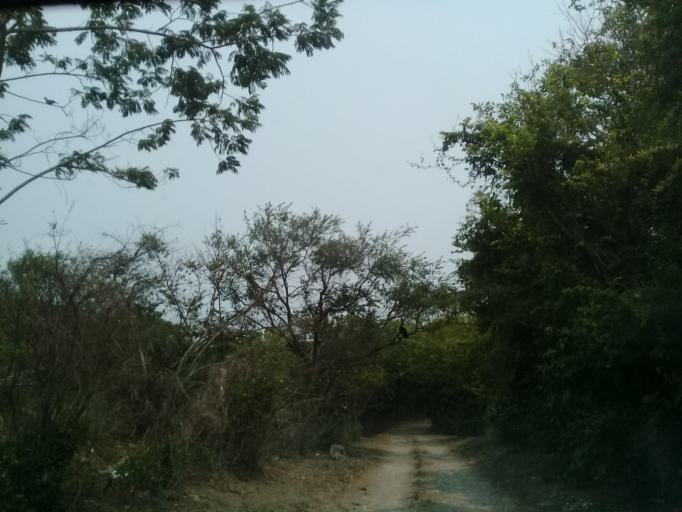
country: MX
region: Veracruz
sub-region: Veracruz
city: Hacienda Sotavento
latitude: 19.1406
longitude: -96.1588
